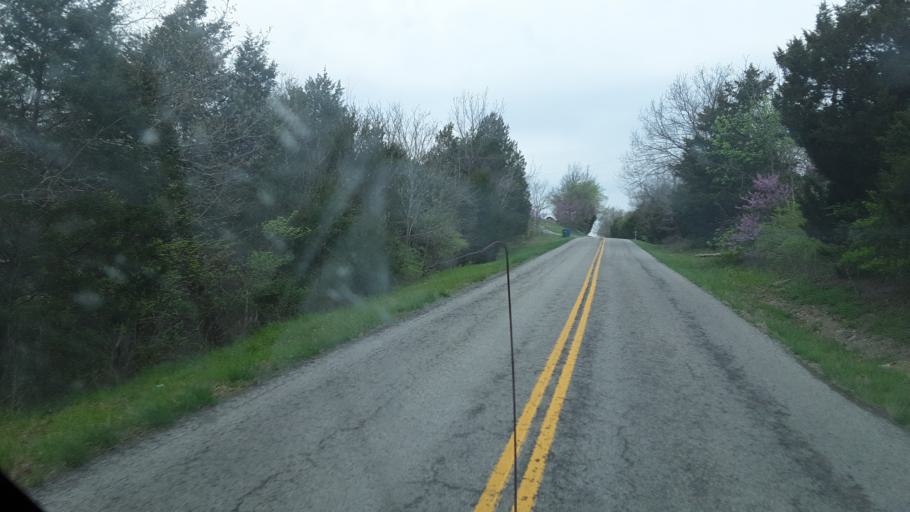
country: US
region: Kentucky
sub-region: Grant County
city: Dry Ridge
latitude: 38.6434
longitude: -84.7244
